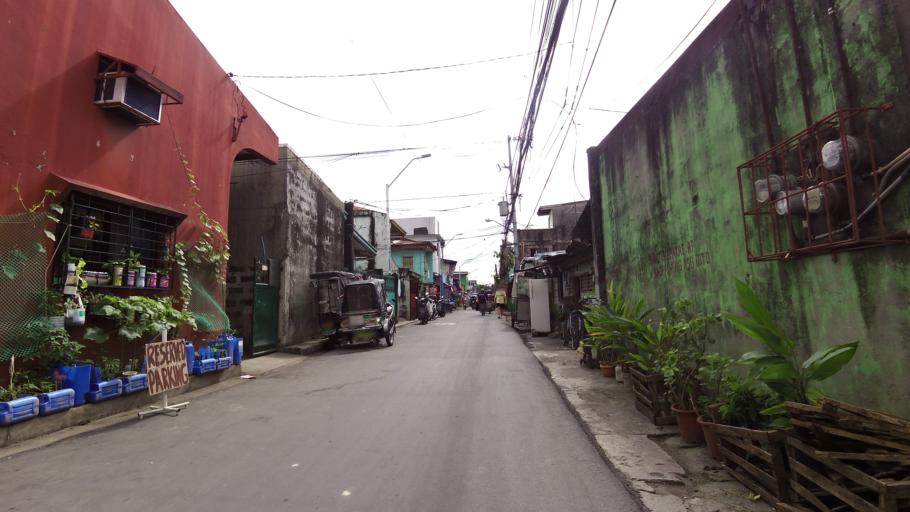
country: PH
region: Calabarzon
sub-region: Province of Rizal
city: Cainta
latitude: 14.5722
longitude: 121.1224
